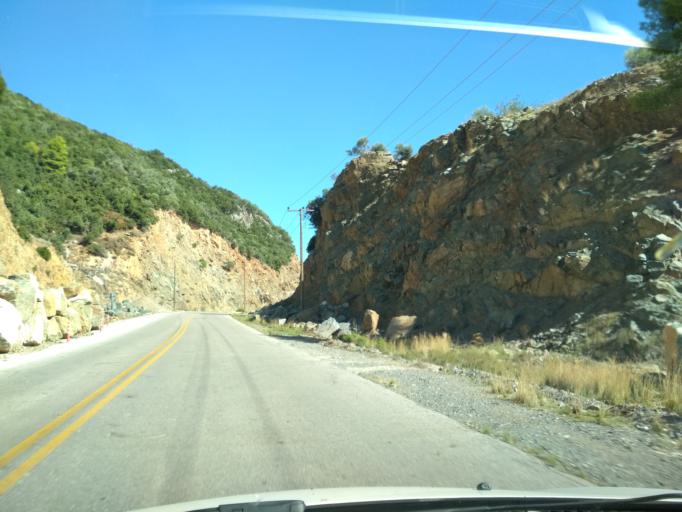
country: GR
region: Central Greece
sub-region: Nomos Evvoias
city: Roviai
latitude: 38.8509
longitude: 23.1468
